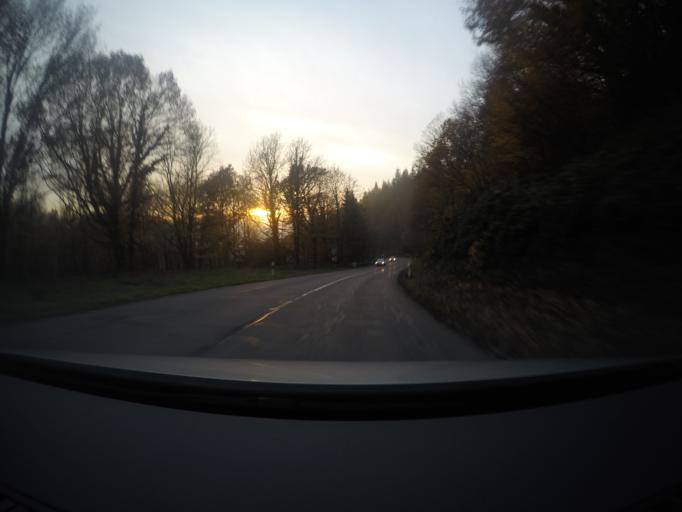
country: DE
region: Baden-Wuerttemberg
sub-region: Karlsruhe Region
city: Baden-Baden
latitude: 48.7727
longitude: 8.2703
